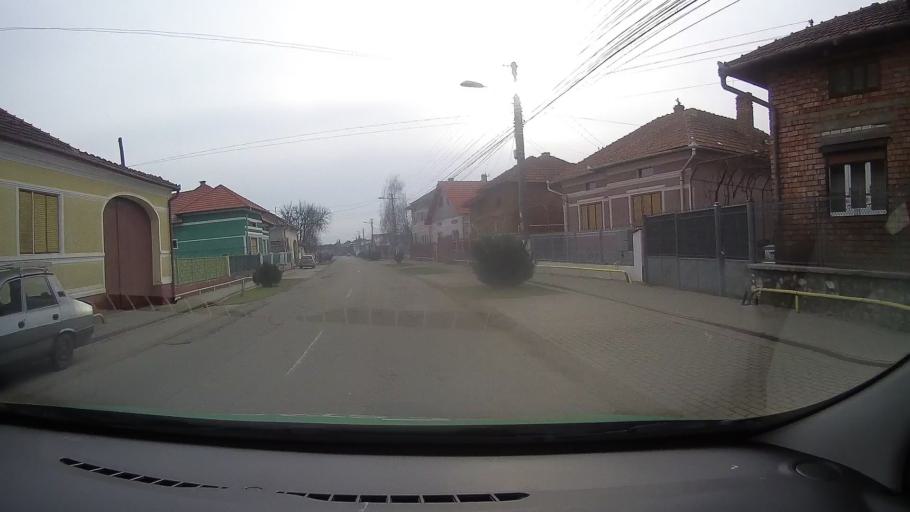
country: RO
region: Hunedoara
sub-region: Comuna Geoagiu
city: Geoagiu
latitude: 45.9285
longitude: 23.1960
